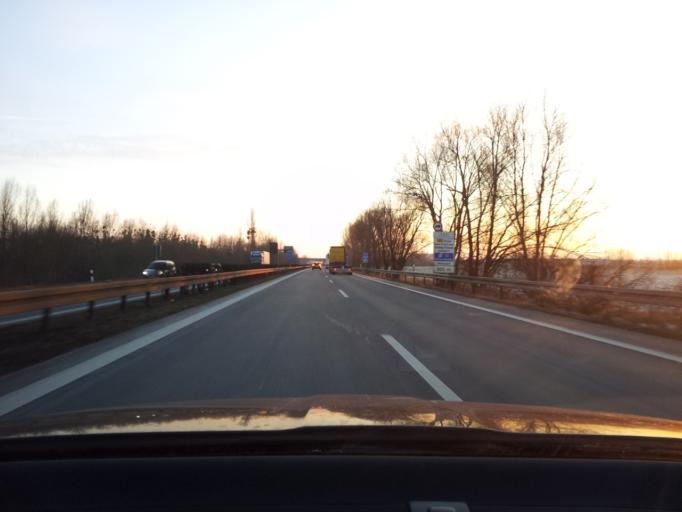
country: DE
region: Brandenburg
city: Wustermark
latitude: 52.5664
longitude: 12.9701
